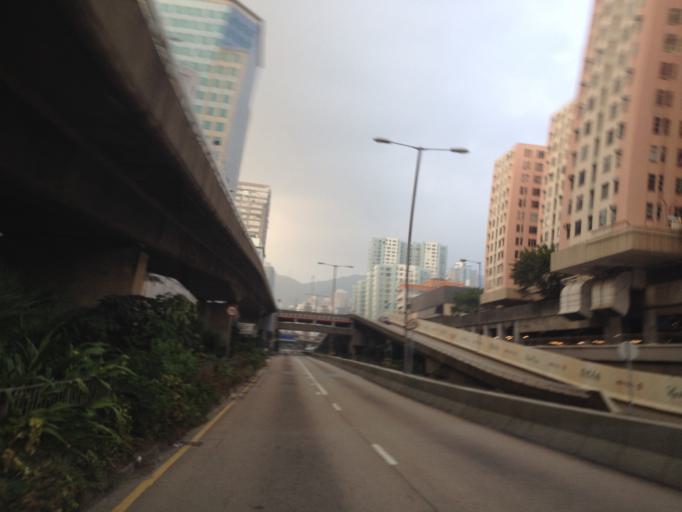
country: HK
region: Kowloon City
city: Kowloon
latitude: 22.3212
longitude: 114.2116
